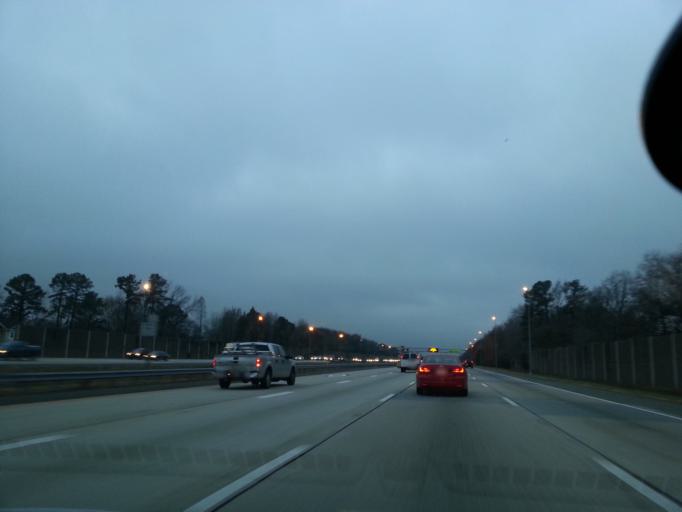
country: US
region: Virginia
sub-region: City of Chesapeake
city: Chesapeake
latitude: 36.7919
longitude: -76.2186
